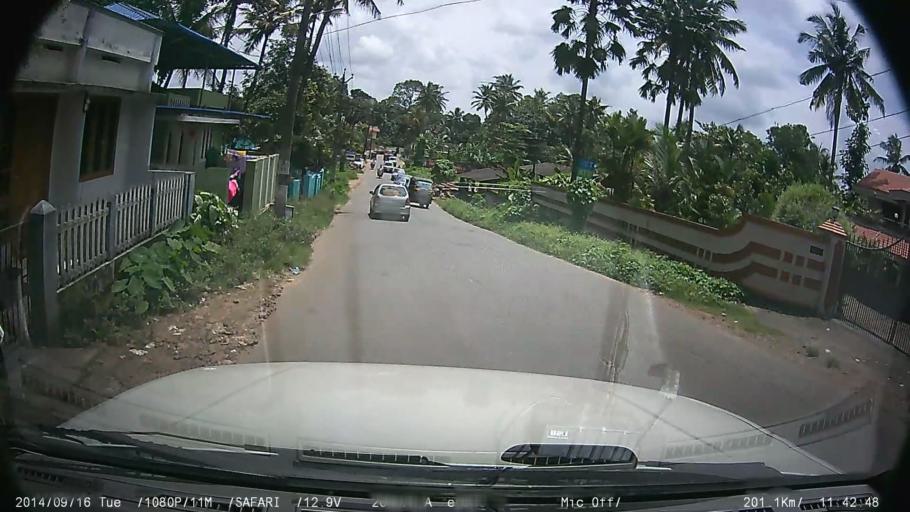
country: IN
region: Kerala
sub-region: Kottayam
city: Changanacheri
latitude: 9.4422
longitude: 76.5568
